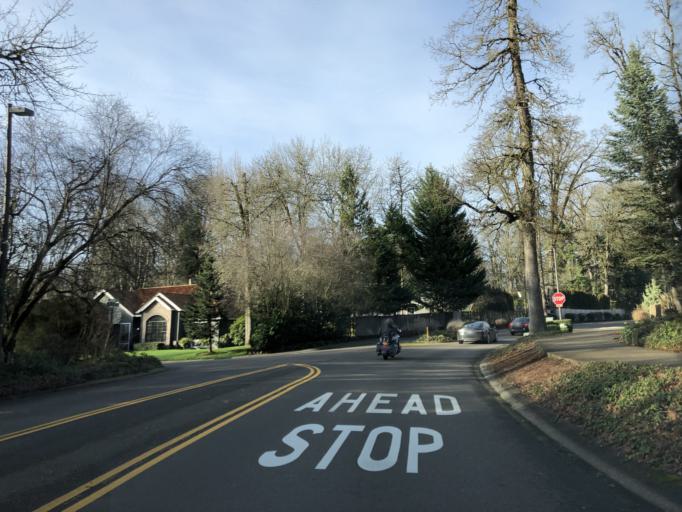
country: US
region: Oregon
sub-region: Washington County
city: Durham
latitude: 45.4203
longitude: -122.7325
